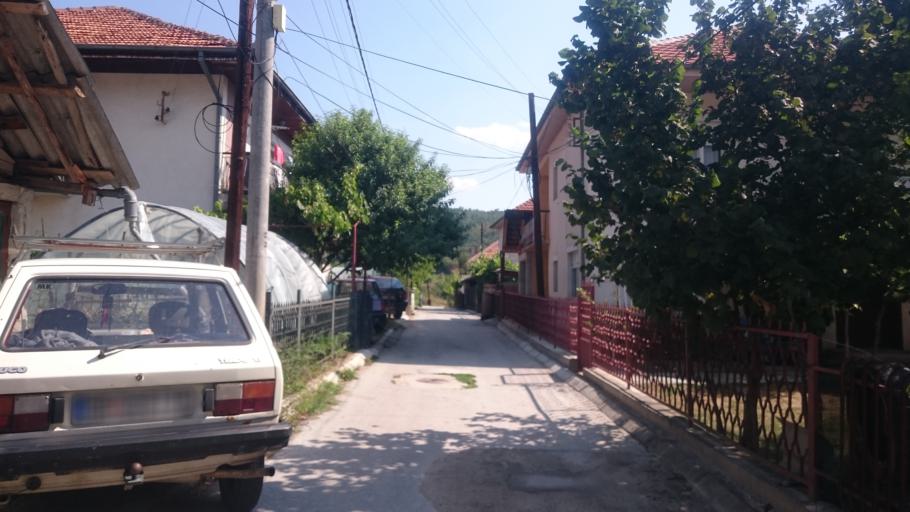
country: MK
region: Makedonski Brod
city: Makedonski Brod
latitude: 41.5134
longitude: 21.2196
